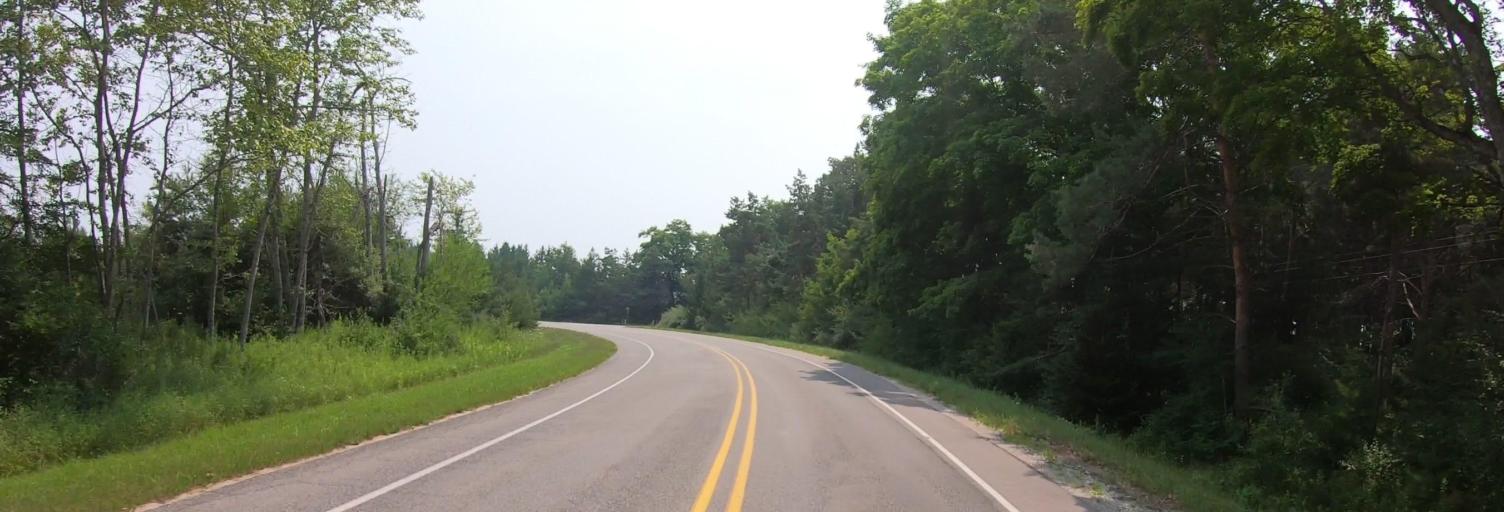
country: US
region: Michigan
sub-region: Leelanau County
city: Leland
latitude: 45.1915
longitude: -85.5454
